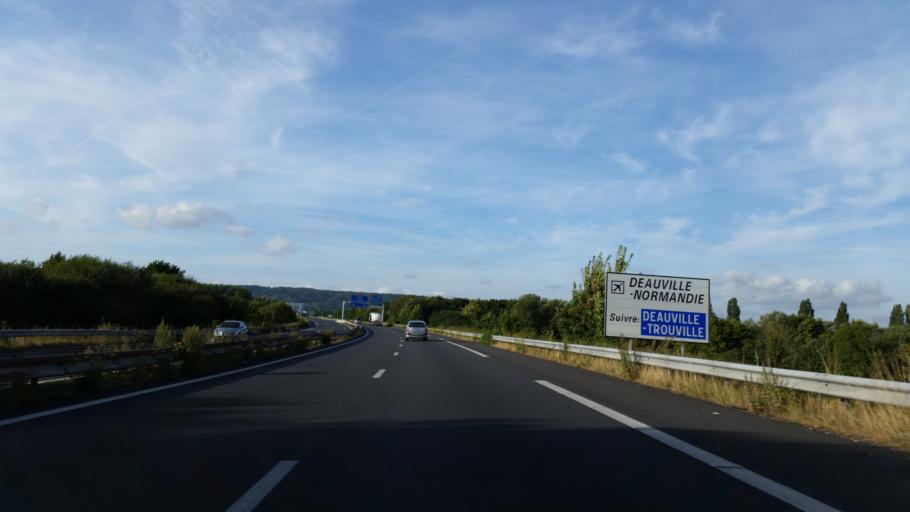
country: FR
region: Lower Normandy
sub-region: Departement du Calvados
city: Saint-Gatien-des-Bois
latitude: 49.2784
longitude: 0.1946
